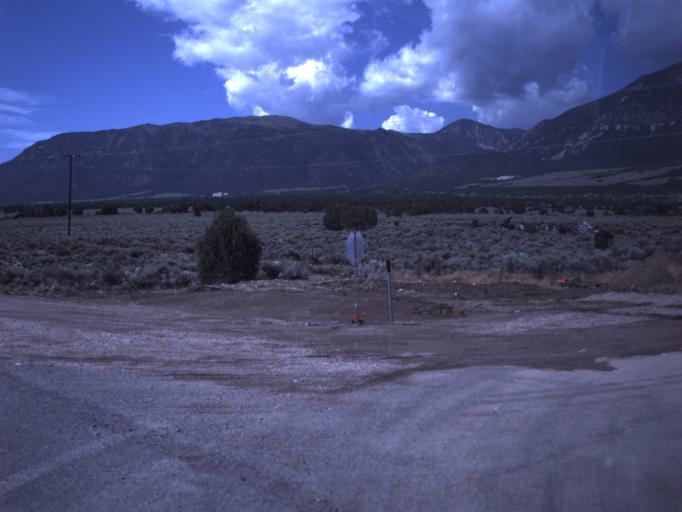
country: US
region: Utah
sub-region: Piute County
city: Junction
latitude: 38.4016
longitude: -112.2312
